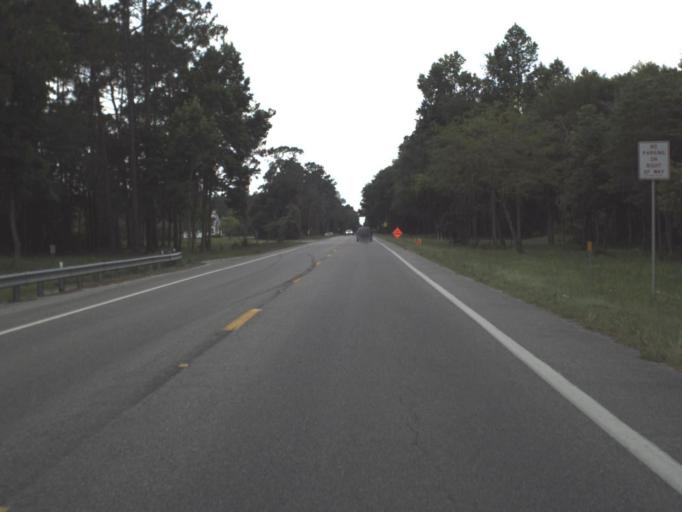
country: US
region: Florida
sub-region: Hamilton County
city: Jasper
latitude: 30.5243
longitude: -82.9794
